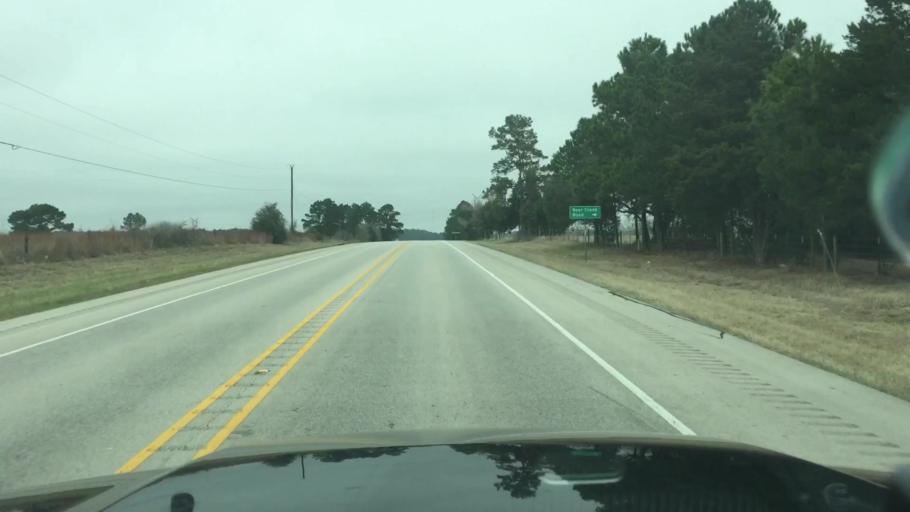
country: US
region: Texas
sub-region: Fayette County
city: La Grange
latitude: 30.0236
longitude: -96.9016
